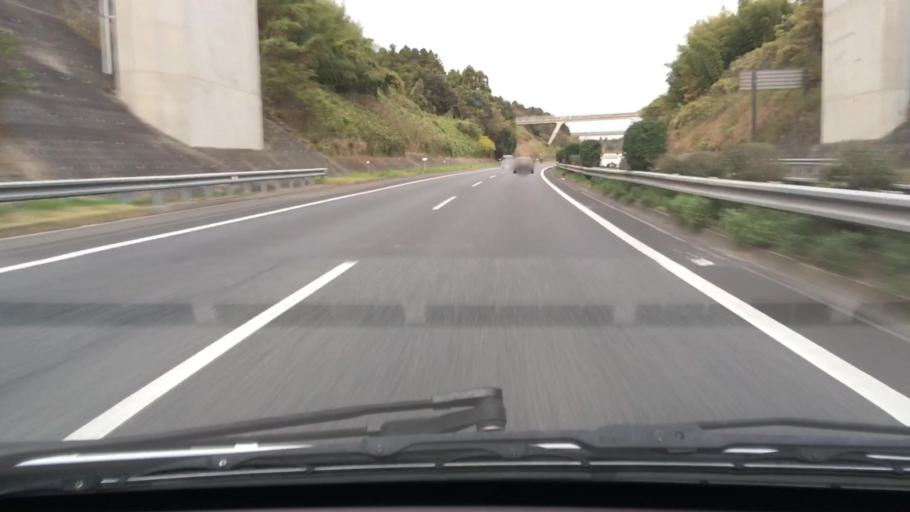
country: JP
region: Chiba
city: Ichihara
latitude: 35.4408
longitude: 140.0597
